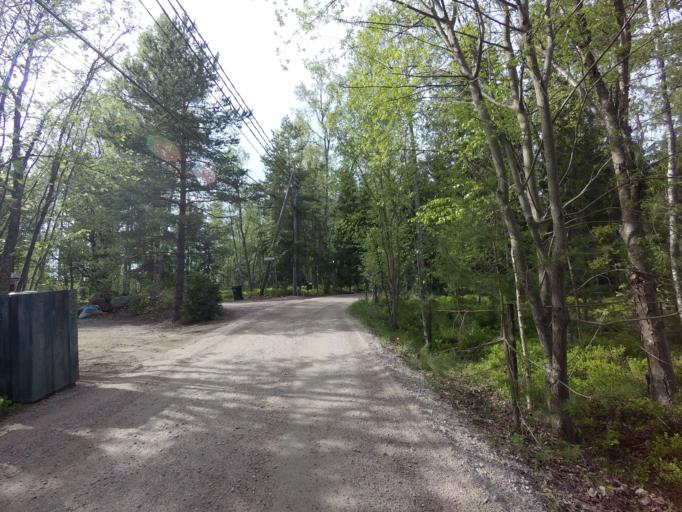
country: FI
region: Uusimaa
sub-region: Helsinki
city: Koukkuniemi
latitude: 60.1245
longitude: 24.7386
